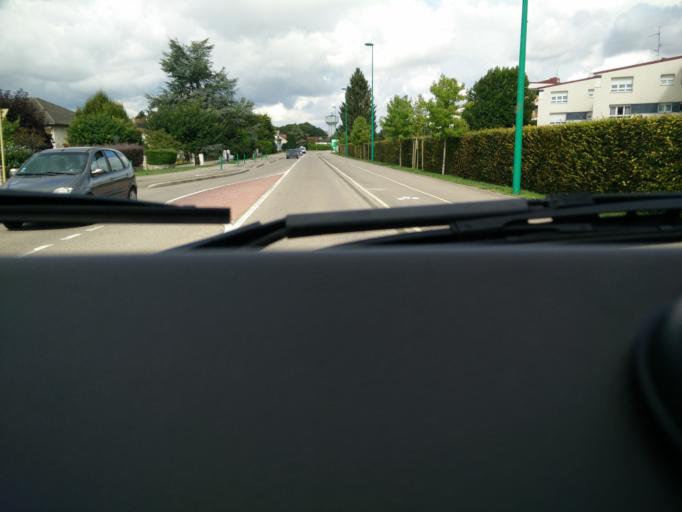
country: FR
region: Lorraine
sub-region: Departement de la Meuse
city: Verdun
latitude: 49.1494
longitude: 5.3999
